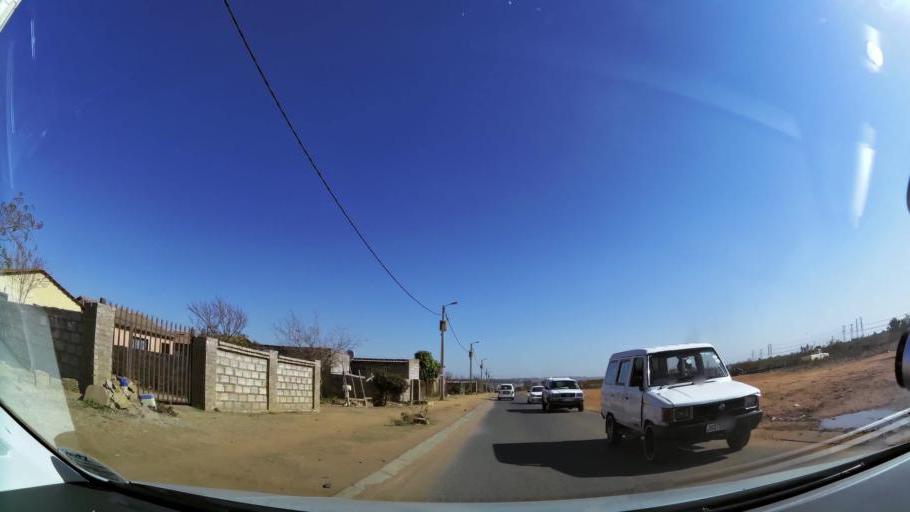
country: ZA
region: Gauteng
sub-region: Ekurhuleni Metropolitan Municipality
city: Tembisa
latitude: -26.0305
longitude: 28.2322
